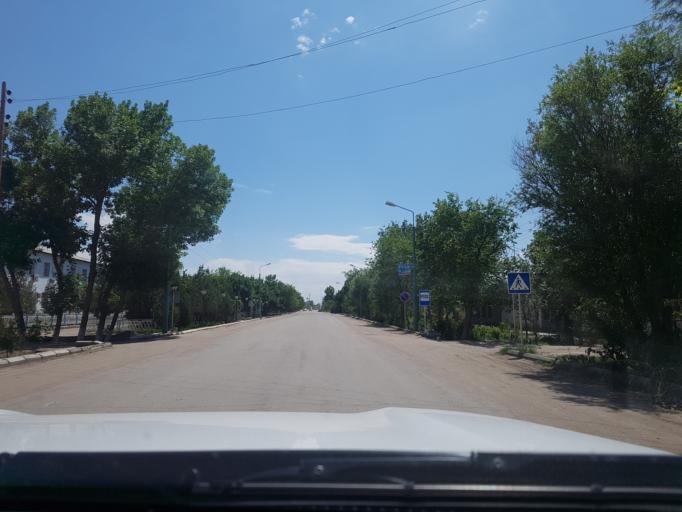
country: TM
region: Dasoguz
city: Dasoguz
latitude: 41.8363
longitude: 60.1319
